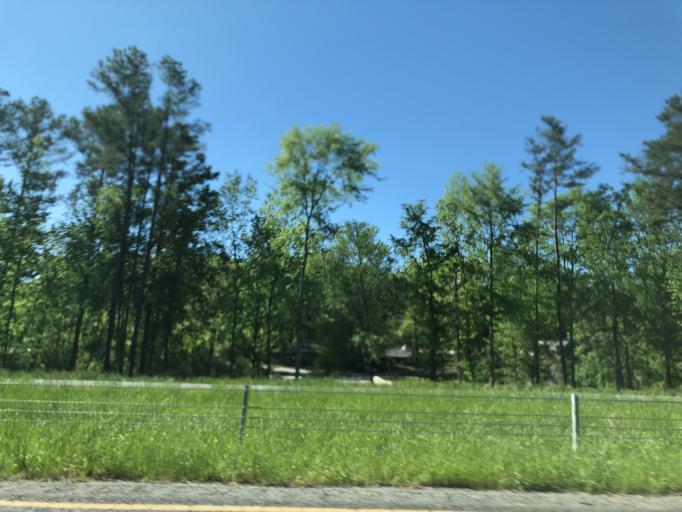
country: US
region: Georgia
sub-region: Clarke County
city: Country Club Estates
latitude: 33.9609
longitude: -83.4318
